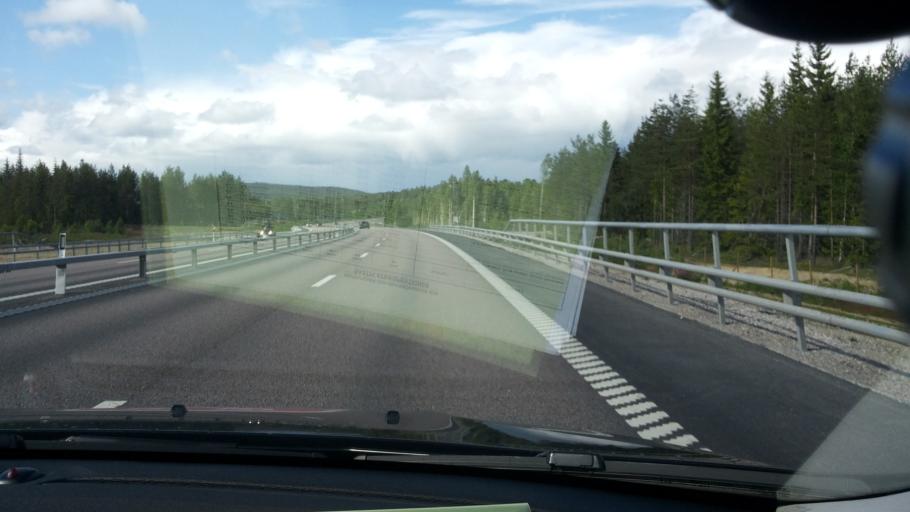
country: SE
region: Vaesternorrland
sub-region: Sundsvalls Kommun
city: Nolby
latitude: 62.2749
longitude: 17.3451
